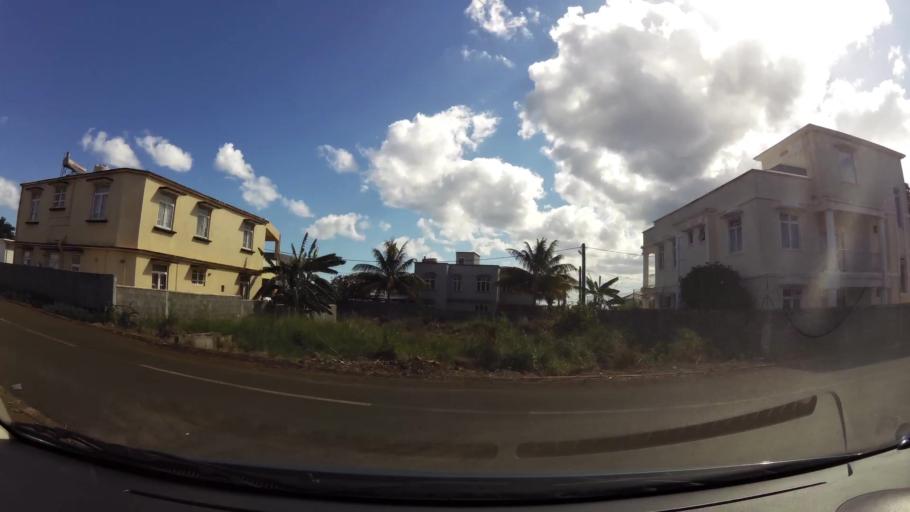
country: MU
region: Black River
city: Albion
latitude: -20.2230
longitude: 57.4165
